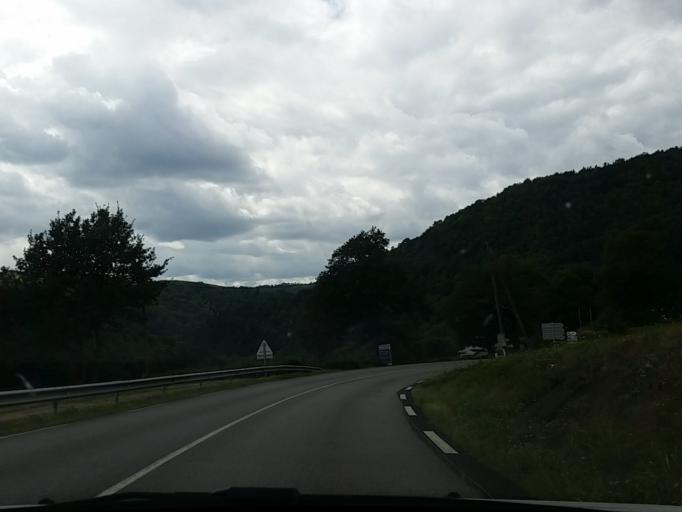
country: FR
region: Auvergne
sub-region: Departement du Cantal
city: Neuveglise
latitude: 44.8936
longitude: 3.0032
